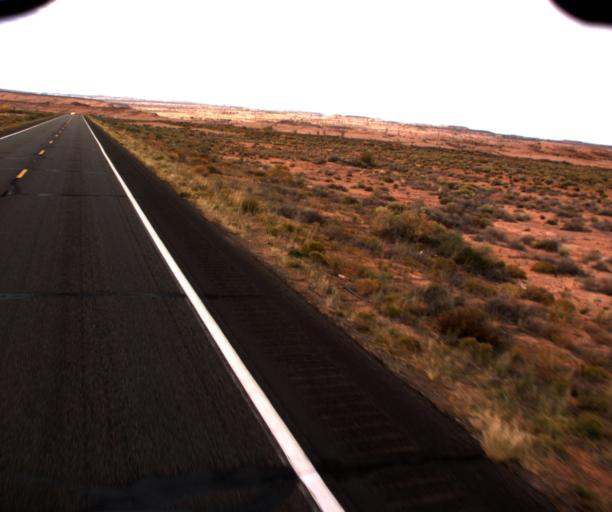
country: US
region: Arizona
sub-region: Apache County
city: Many Farms
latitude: 36.9392
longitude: -109.6889
